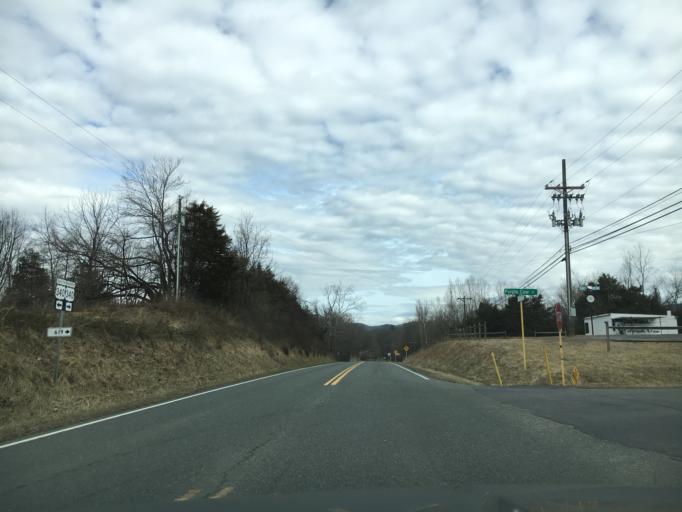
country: US
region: Virginia
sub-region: Augusta County
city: Dooms
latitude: 38.1256
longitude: -78.8494
